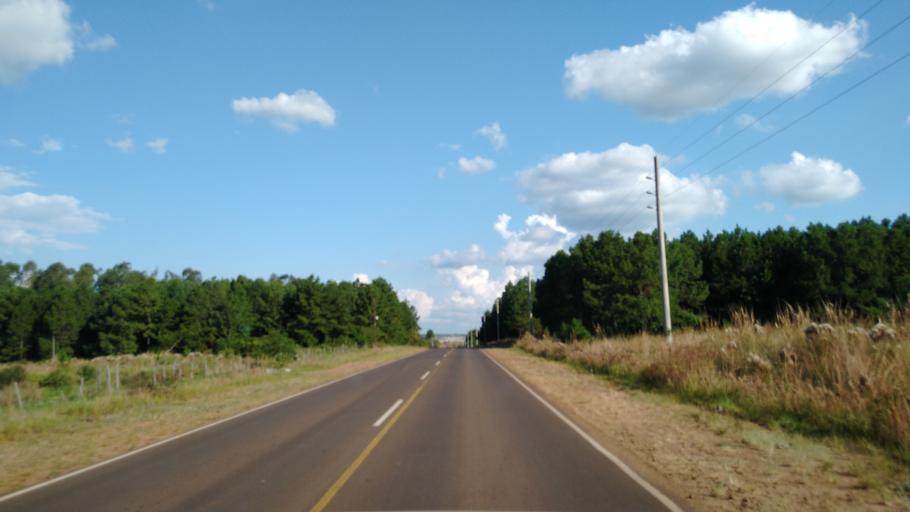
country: PY
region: Itapua
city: San Juan del Parana
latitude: -27.3812
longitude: -55.9917
